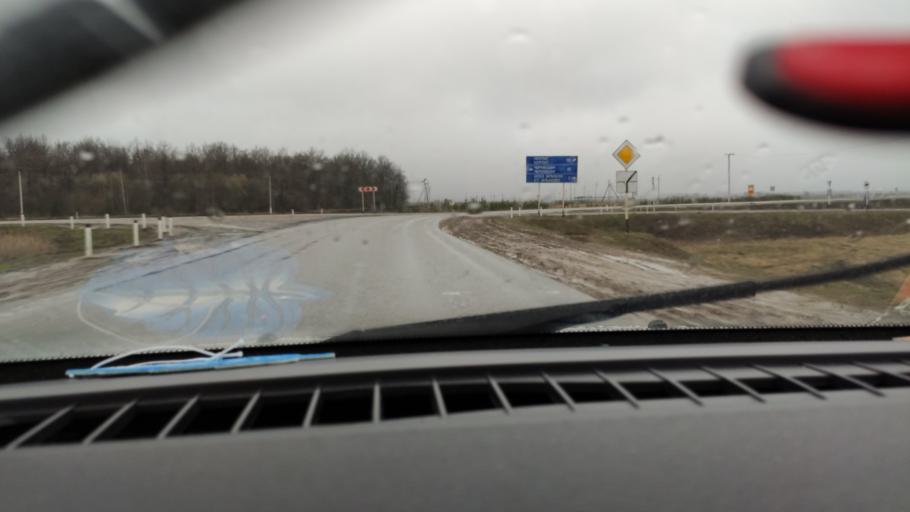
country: RU
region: Tatarstan
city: Cheremshan
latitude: 54.7321
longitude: 51.3298
